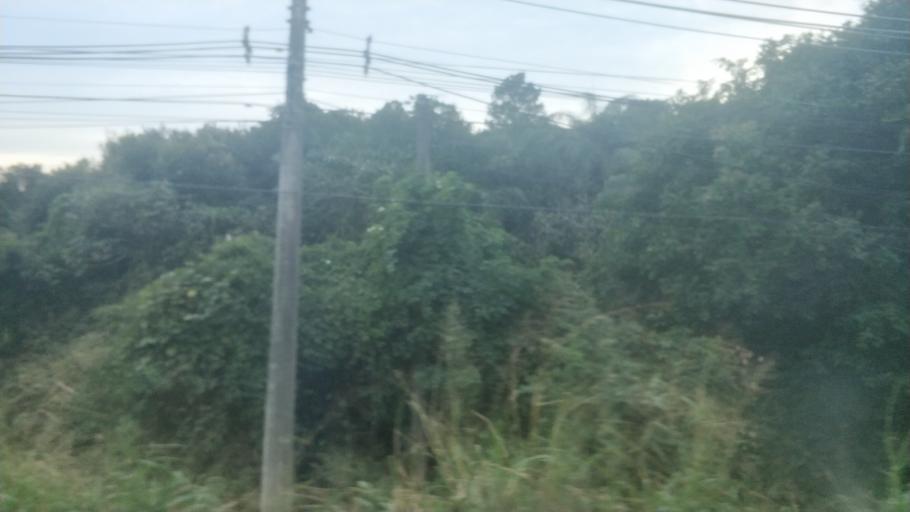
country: BR
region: Rio de Janeiro
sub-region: Seropedica
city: Seropedica
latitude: -22.7530
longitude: -43.6940
